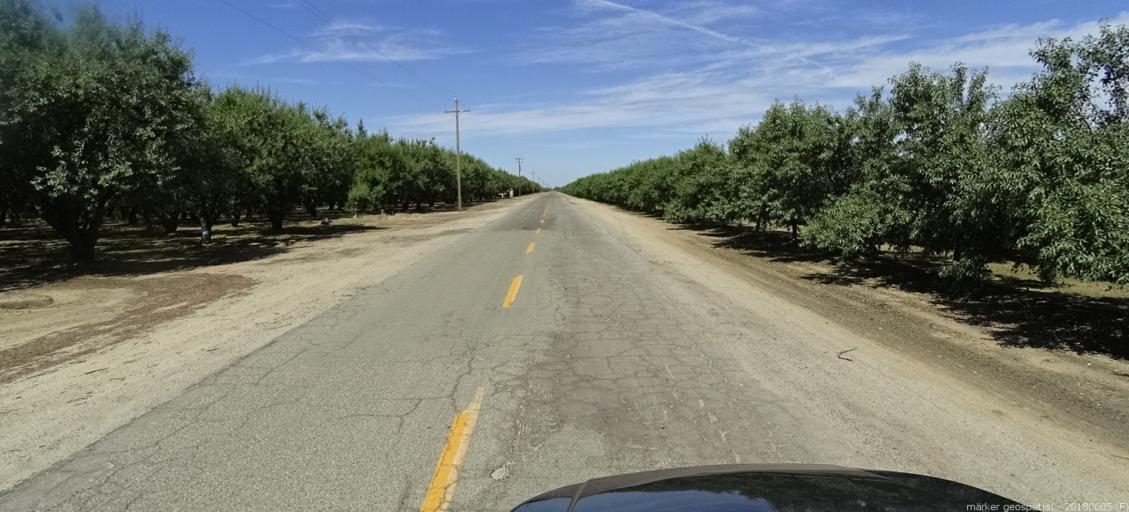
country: US
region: California
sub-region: Madera County
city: Chowchilla
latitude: 37.0983
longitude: -120.4125
